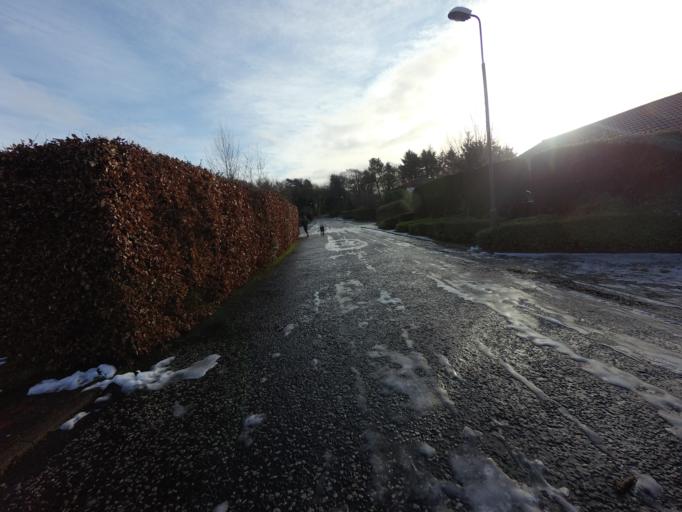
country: GB
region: Scotland
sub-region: West Lothian
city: Livingston
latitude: 55.9097
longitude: -3.5608
